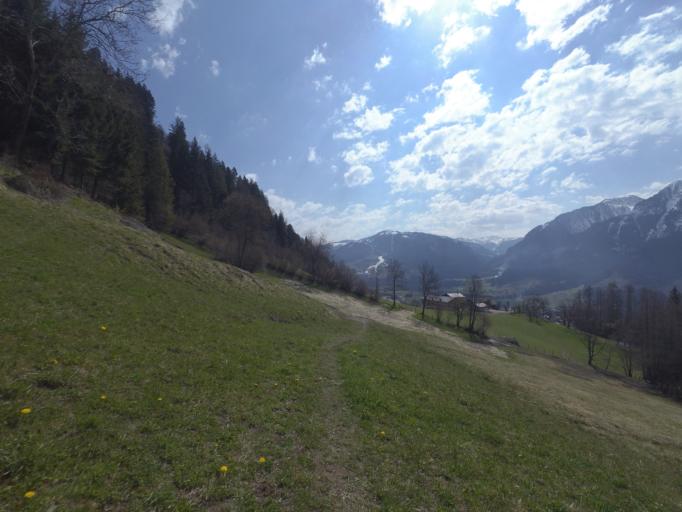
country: AT
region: Salzburg
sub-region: Politischer Bezirk Sankt Johann im Pongau
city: Sankt Veit im Pongau
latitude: 47.3371
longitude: 13.1448
